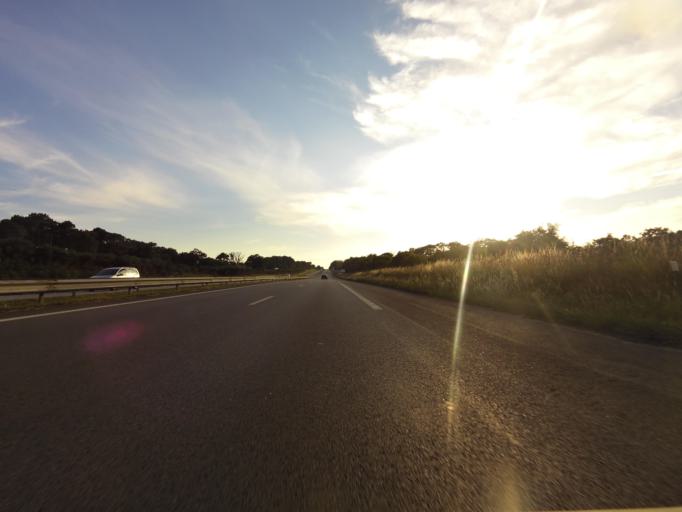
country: FR
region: Brittany
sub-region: Departement du Morbihan
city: Ploeren
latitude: 47.6616
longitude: -2.8396
